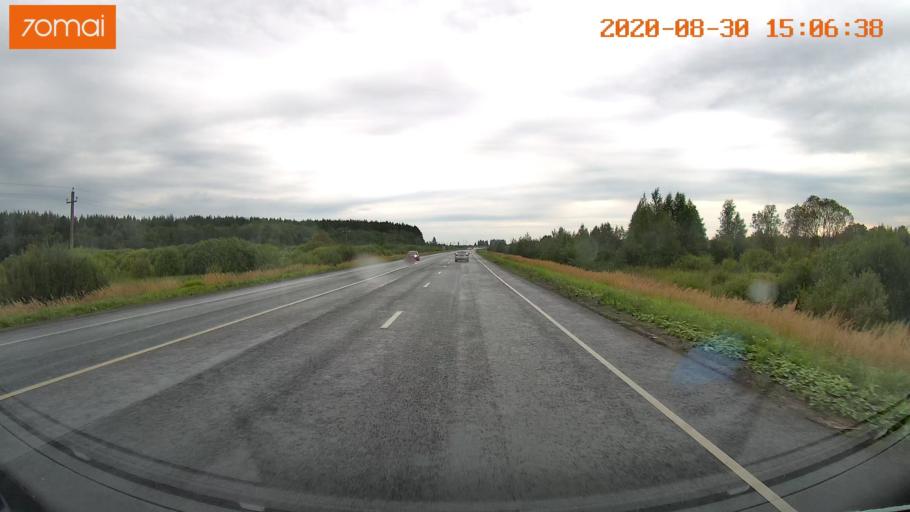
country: RU
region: Ivanovo
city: Staraya Vichuga
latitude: 57.2561
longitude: 41.9013
